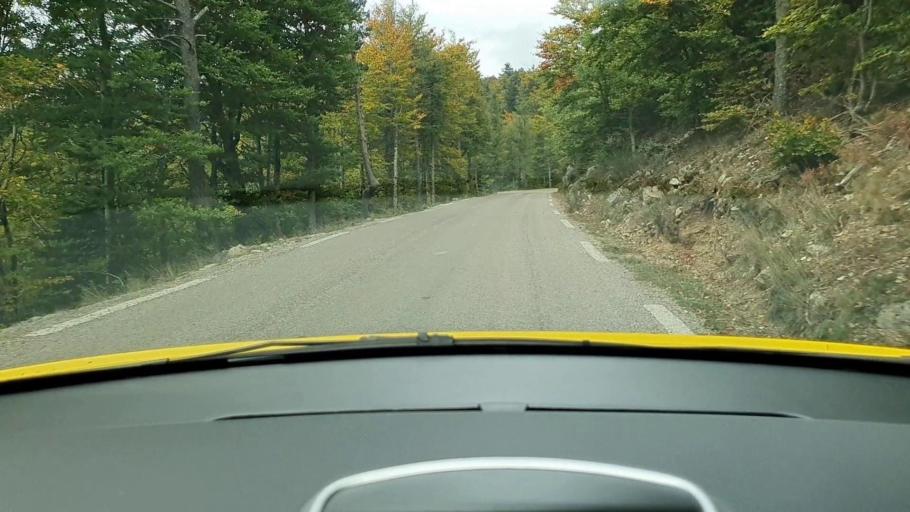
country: FR
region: Languedoc-Roussillon
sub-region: Departement du Gard
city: Le Vigan
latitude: 44.0526
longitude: 3.5509
